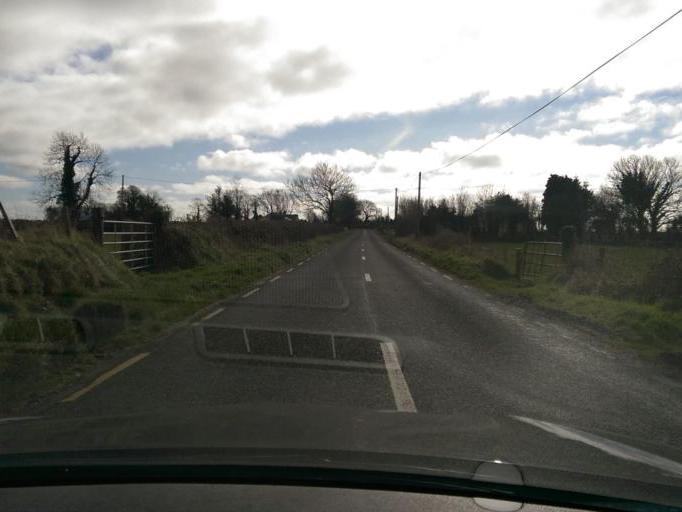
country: IE
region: Connaught
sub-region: County Galway
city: Ballinasloe
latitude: 53.4259
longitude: -8.4090
